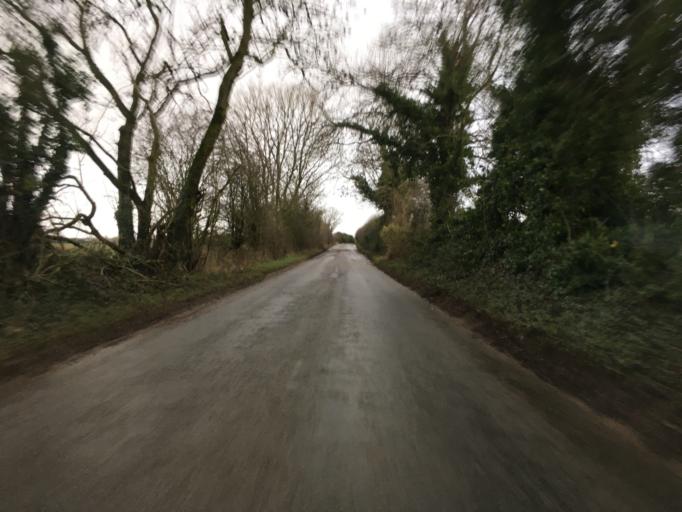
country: GB
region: England
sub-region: South Gloucestershire
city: Marshfield
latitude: 51.4939
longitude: -2.3424
